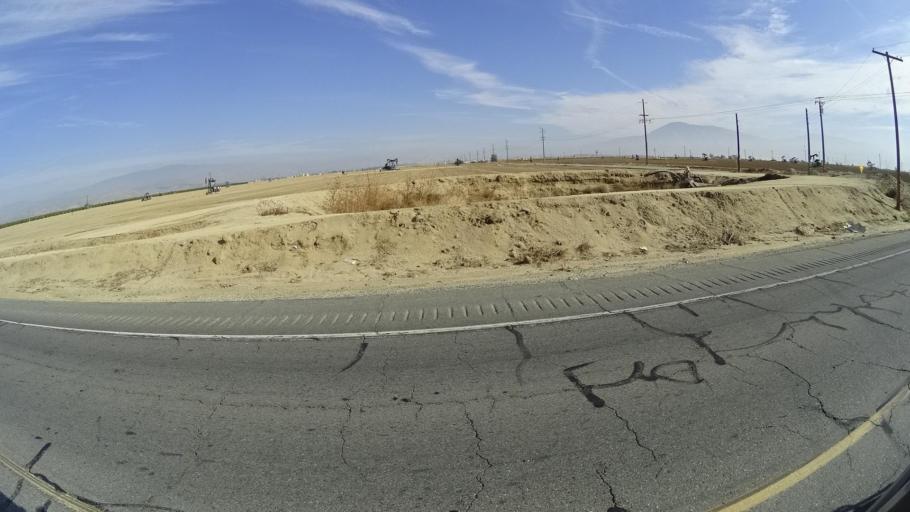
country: US
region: California
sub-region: Kern County
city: Lamont
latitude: 35.3116
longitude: -118.8430
